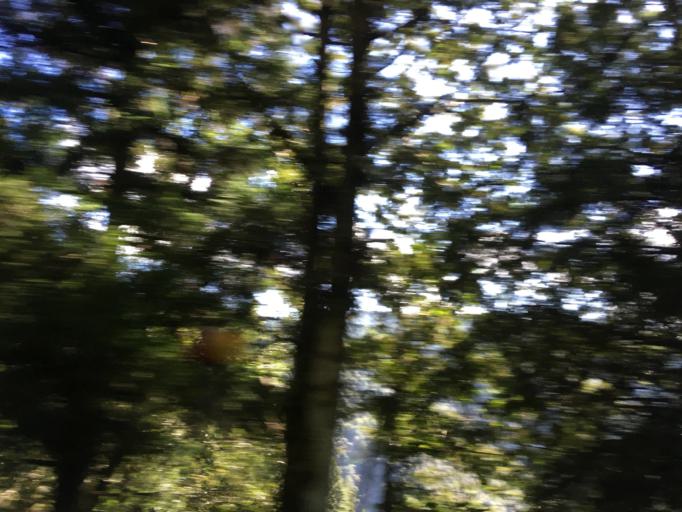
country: TW
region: Taiwan
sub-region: Yilan
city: Yilan
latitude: 24.5060
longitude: 121.5695
